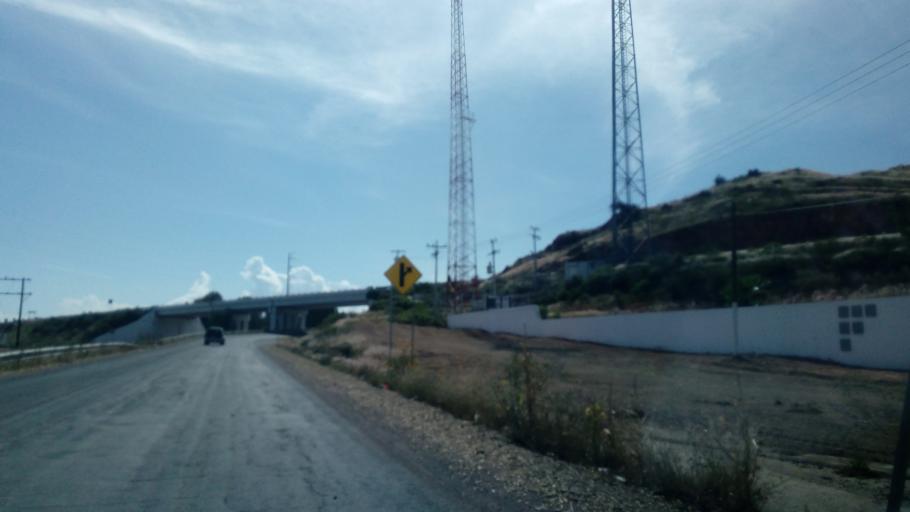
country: MX
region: Durango
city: Victoria de Durango
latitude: 24.0706
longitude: -104.6557
